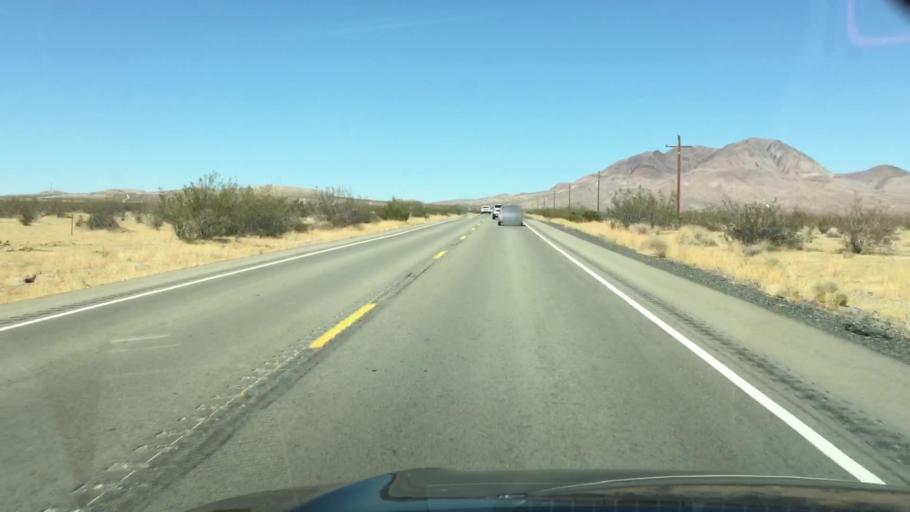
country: US
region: California
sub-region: Kern County
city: Boron
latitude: 35.2917
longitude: -117.6153
